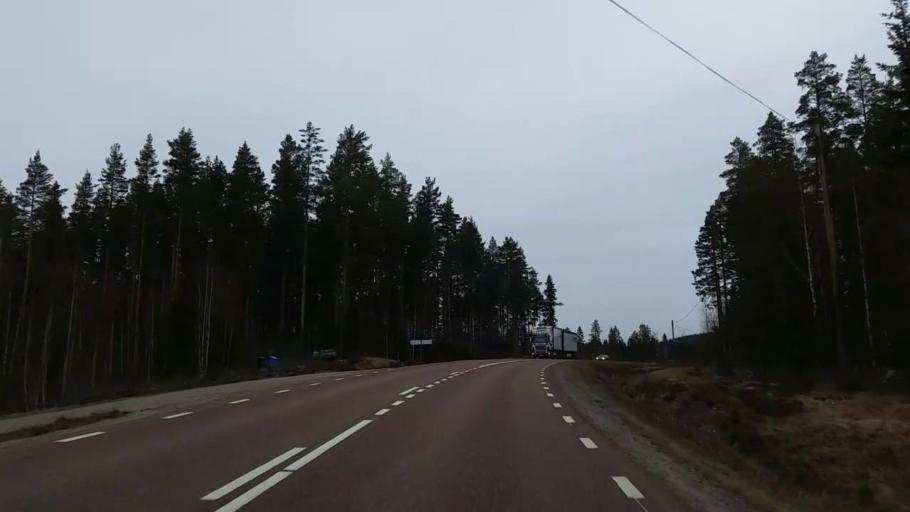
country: SE
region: Gaevleborg
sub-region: Ovanakers Kommun
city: Edsbyn
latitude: 61.2114
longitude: 15.8712
